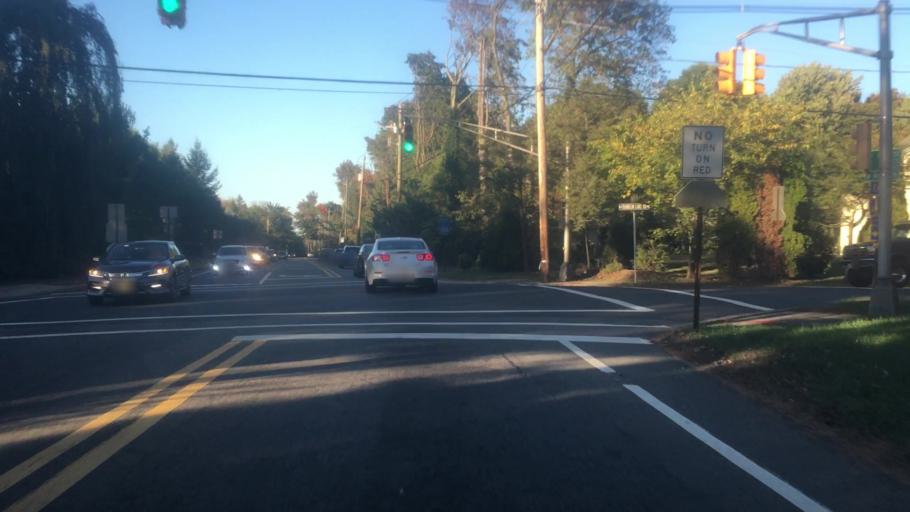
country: US
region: New Jersey
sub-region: Bergen County
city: Franklin Lakes
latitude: 40.9944
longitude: -74.1983
